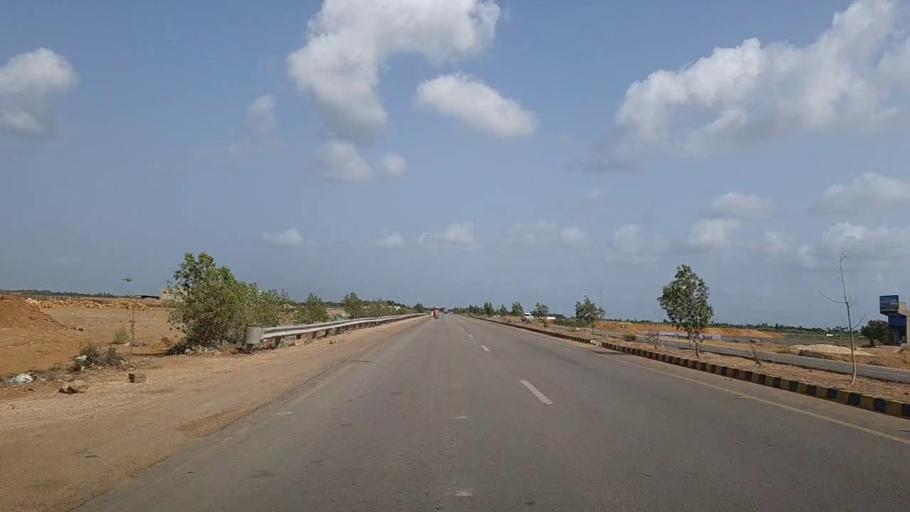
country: PK
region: Sindh
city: Gharo
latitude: 24.7357
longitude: 67.5999
